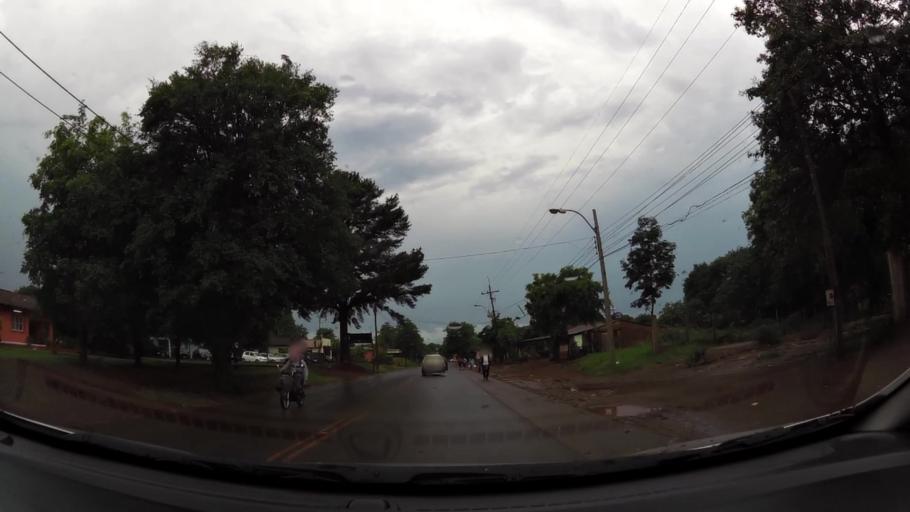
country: PY
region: Alto Parana
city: Presidente Franco
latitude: -25.5561
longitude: -54.6540
